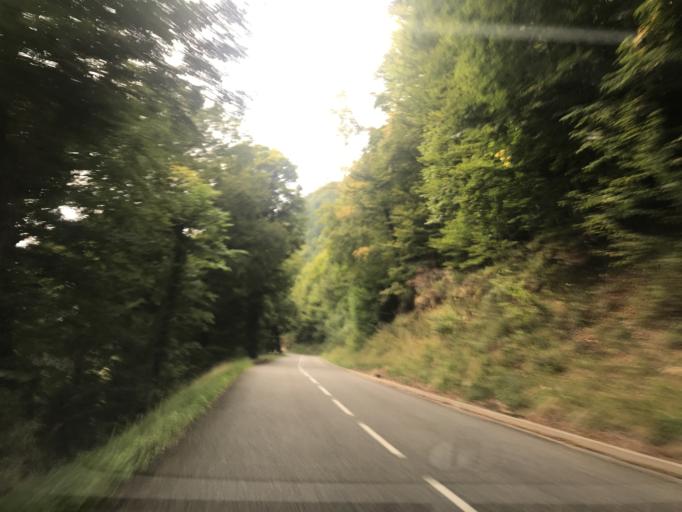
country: FR
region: Midi-Pyrenees
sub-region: Departement de la Haute-Garonne
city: Bagneres-de-Luchon
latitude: 42.7711
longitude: 0.6499
